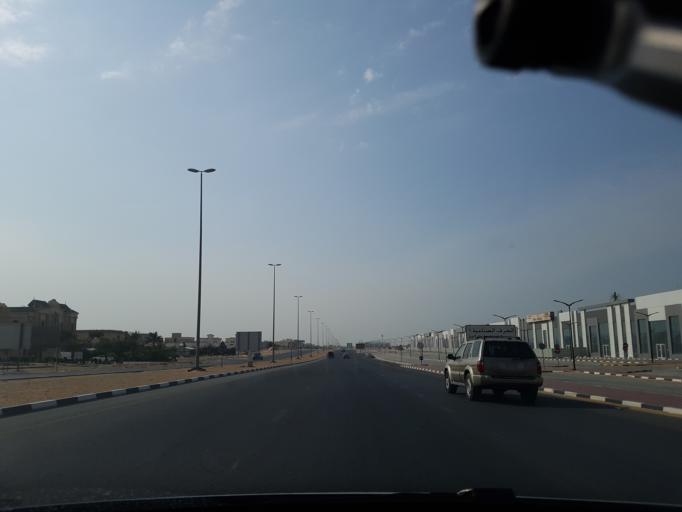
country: AE
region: Ajman
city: Ajman
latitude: 25.4230
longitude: 55.5302
